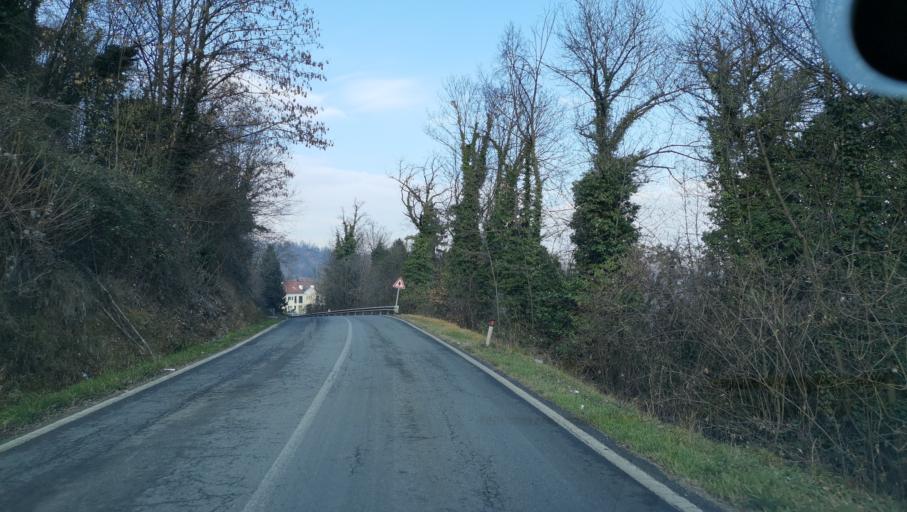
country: IT
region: Piedmont
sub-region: Provincia di Torino
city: Gassino Torinese
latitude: 45.1024
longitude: 7.8430
